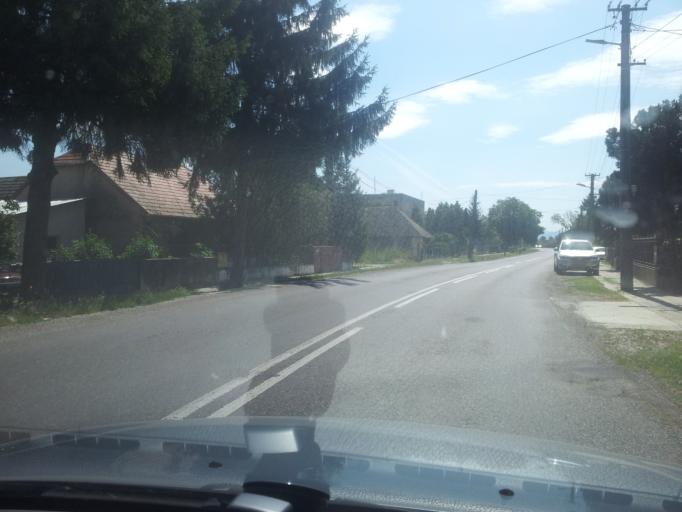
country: SK
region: Nitriansky
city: Zeliezovce
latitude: 48.1118
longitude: 18.6274
